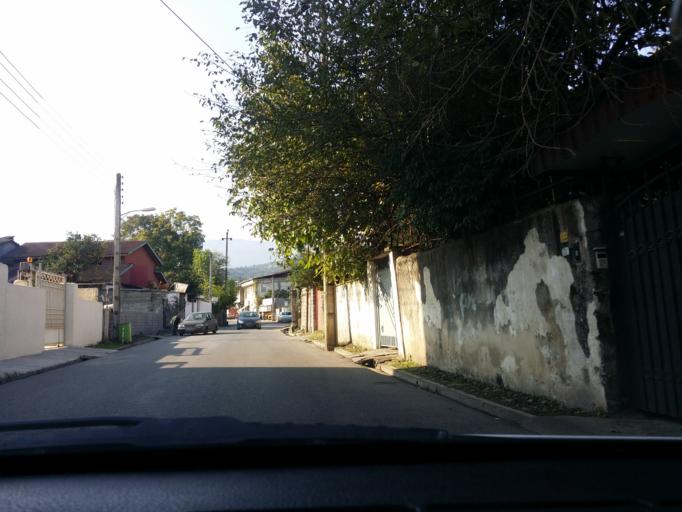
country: IR
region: Mazandaran
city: Chalus
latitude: 36.6527
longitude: 51.4139
